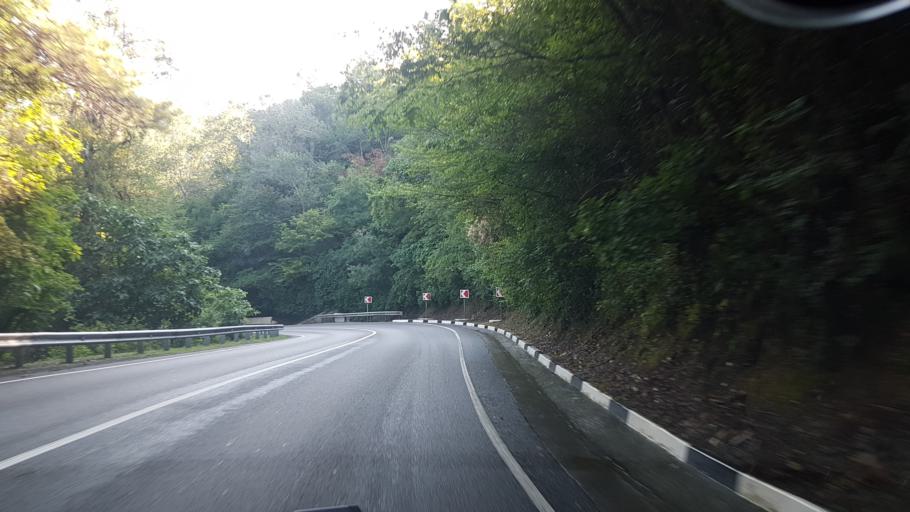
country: RU
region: Krasnodarskiy
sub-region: Sochi City
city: Lazarevskoye
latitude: 43.8232
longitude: 39.4362
